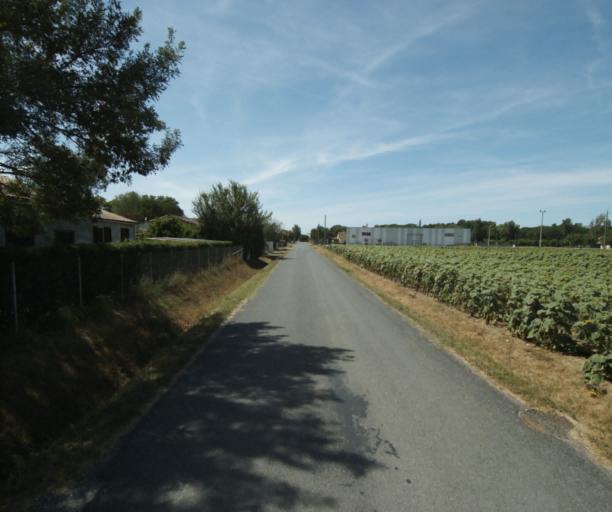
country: FR
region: Midi-Pyrenees
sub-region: Departement du Tarn
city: Puylaurens
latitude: 43.5194
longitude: 2.0126
